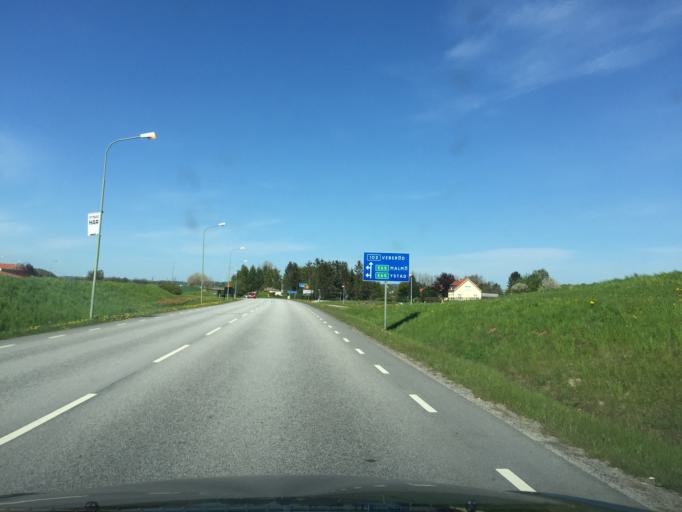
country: SE
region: Skane
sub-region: Skurups Kommun
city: Skurup
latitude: 55.4912
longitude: 13.5074
